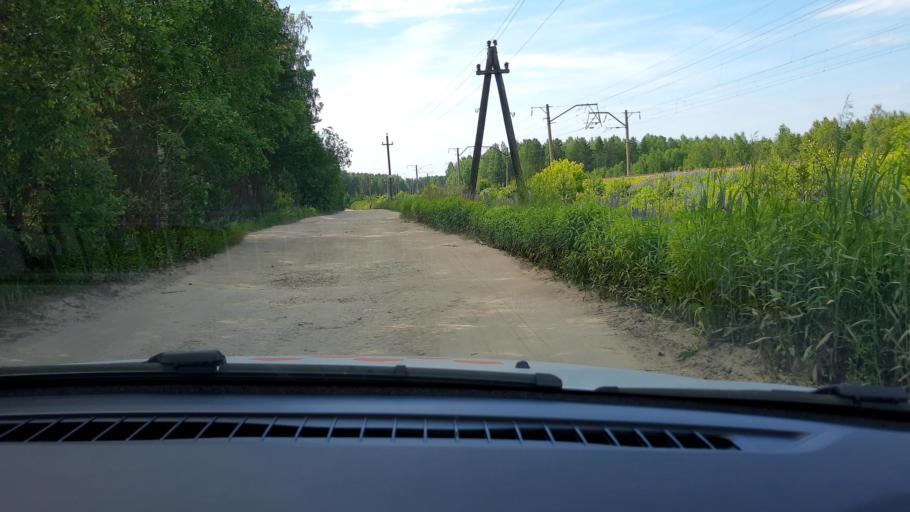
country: RU
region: Nizjnij Novgorod
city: Linda
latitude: 56.6654
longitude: 44.1684
